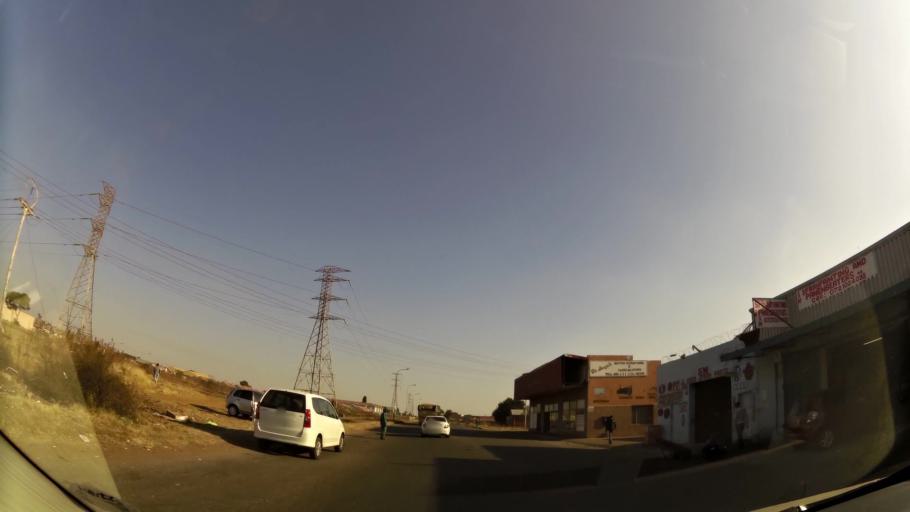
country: ZA
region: Gauteng
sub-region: West Rand District Municipality
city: Randfontein
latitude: -26.1864
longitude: 27.6971
